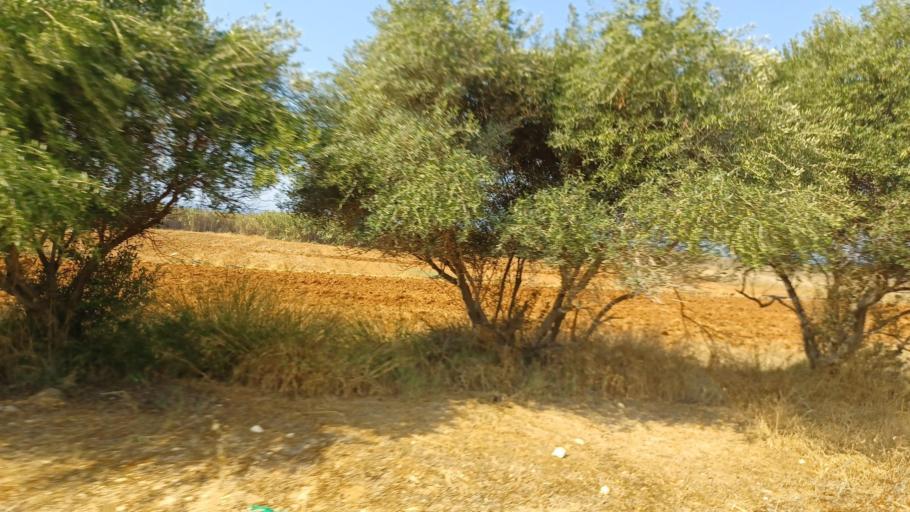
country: CY
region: Larnaka
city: Xylotymbou
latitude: 34.9782
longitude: 33.7881
